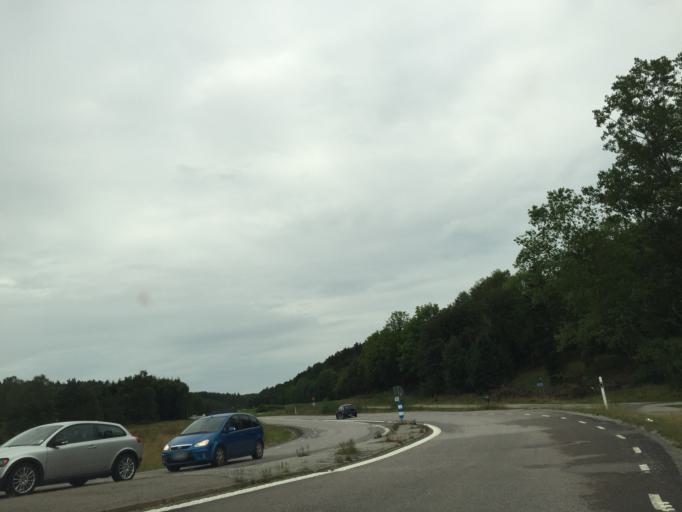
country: SE
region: Vaestra Goetaland
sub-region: Tjorns Kommun
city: Myggenas
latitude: 58.0232
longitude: 11.6955
